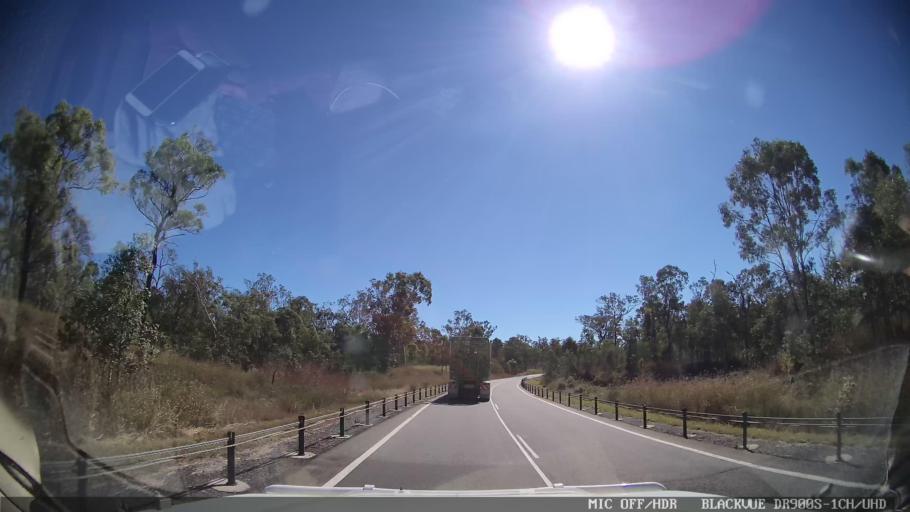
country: AU
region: Queensland
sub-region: Gladstone
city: Toolooa
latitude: -24.1557
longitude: 151.2119
